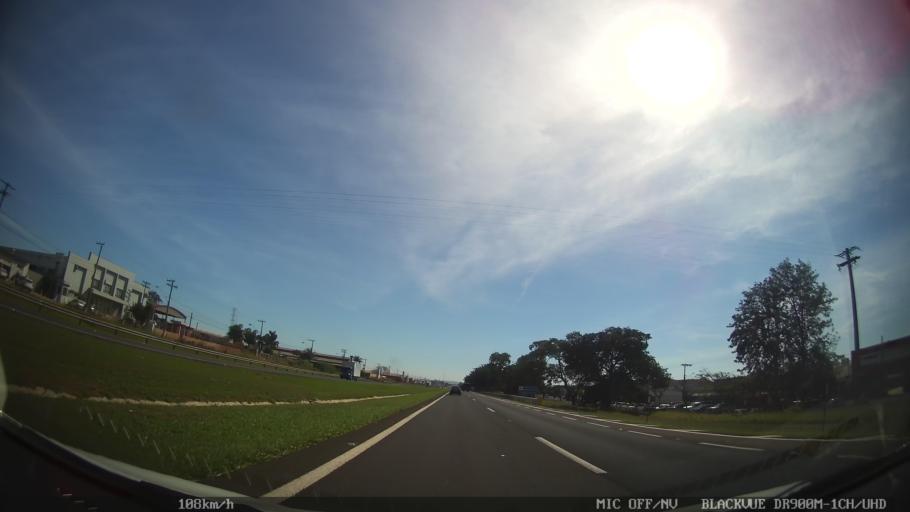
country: BR
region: Sao Paulo
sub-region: Porto Ferreira
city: Porto Ferreira
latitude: -21.8779
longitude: -47.4867
